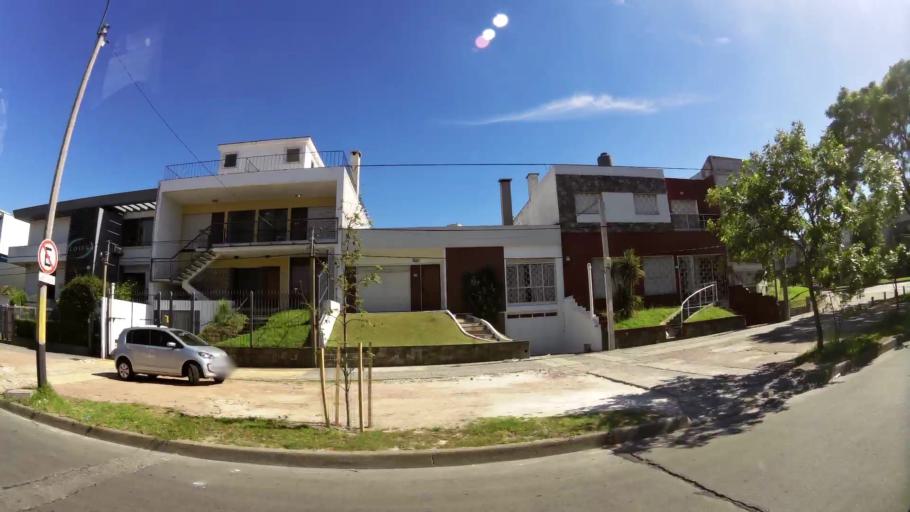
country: UY
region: Montevideo
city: Montevideo
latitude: -34.8961
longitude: -56.1495
